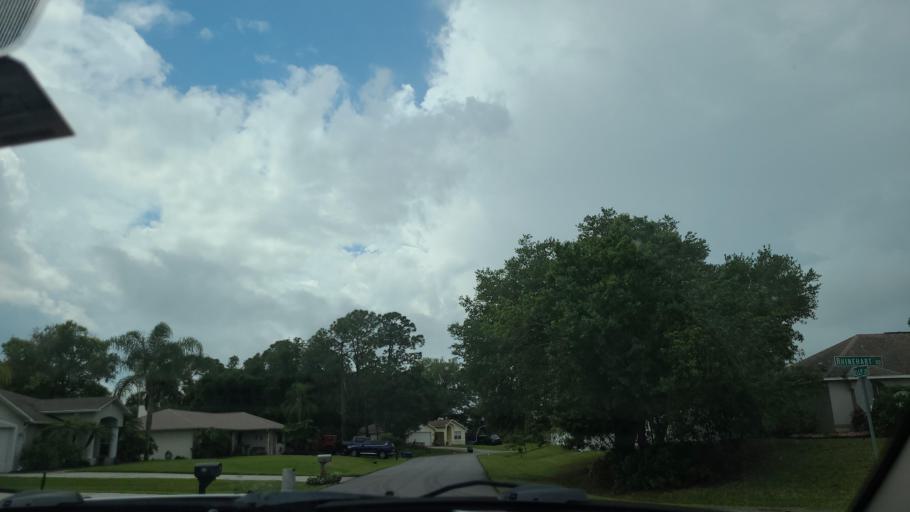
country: US
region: Florida
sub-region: Brevard County
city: Grant-Valkaria
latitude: 27.9348
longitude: -80.6284
